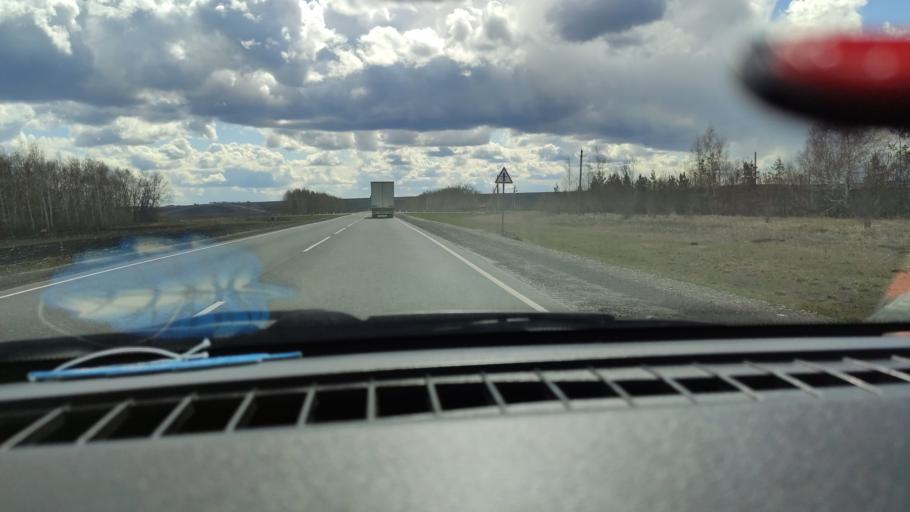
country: RU
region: Samara
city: Syzran'
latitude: 52.9838
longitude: 48.3154
